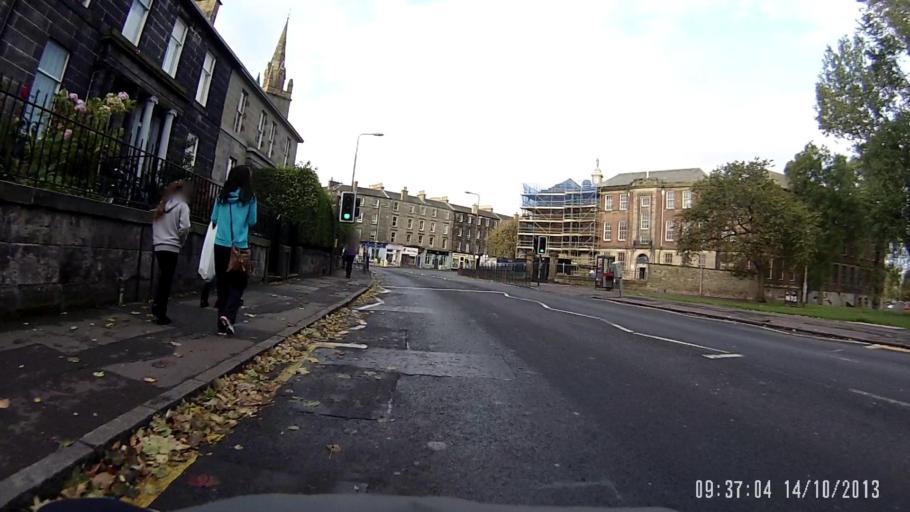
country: GB
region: Scotland
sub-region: West Lothian
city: Seafield
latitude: 55.9691
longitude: -3.1662
